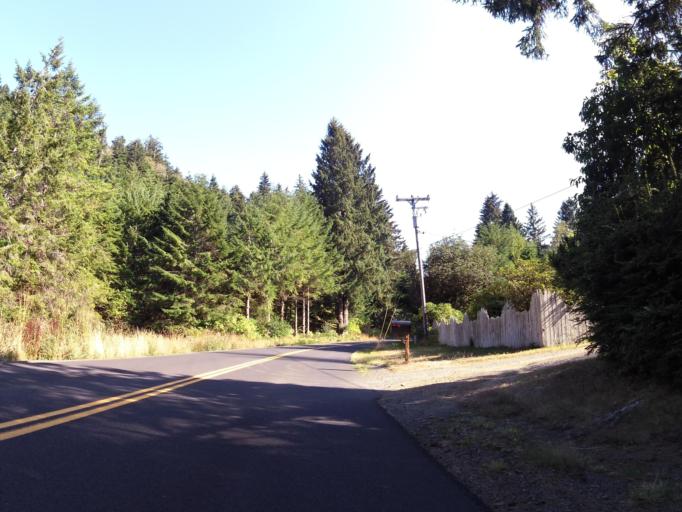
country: US
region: Oregon
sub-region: Lincoln County
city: Rose Lodge
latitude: 45.0825
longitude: -123.9455
